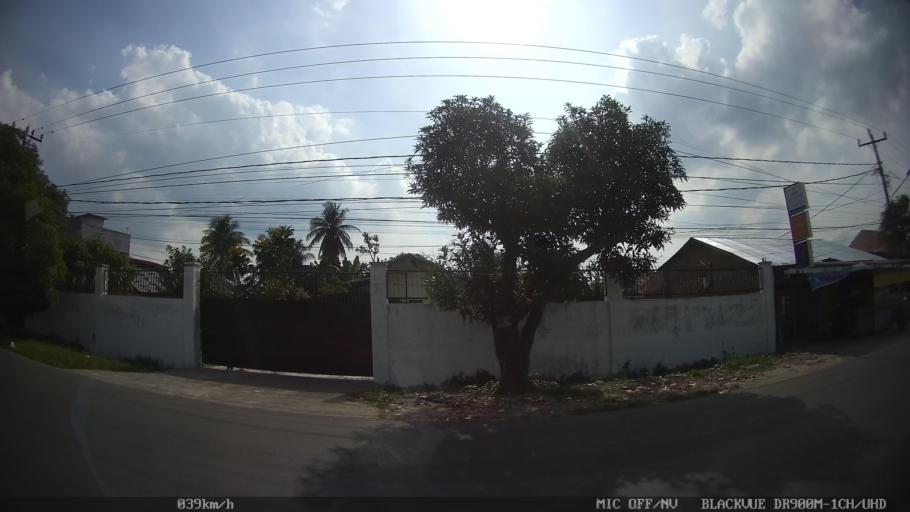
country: ID
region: North Sumatra
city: Binjai
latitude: 3.6227
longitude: 98.4954
